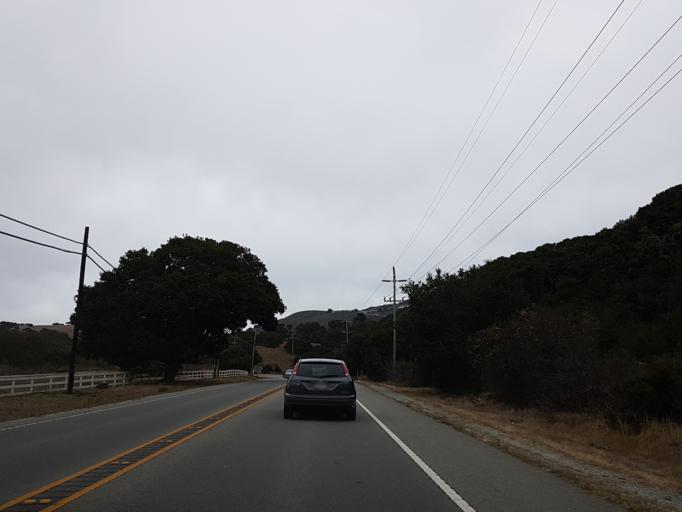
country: US
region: California
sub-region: Monterey County
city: Del Rey Oaks
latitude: 36.5686
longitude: -121.7846
